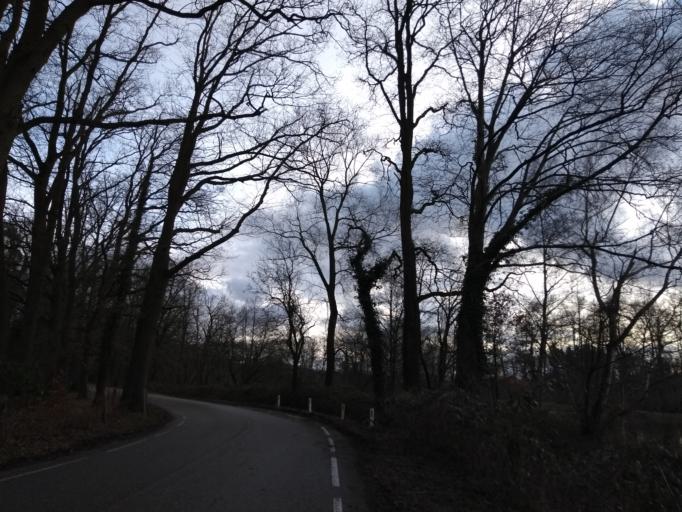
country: NL
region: Overijssel
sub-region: Gemeente Enschede
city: Enschede
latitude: 52.2540
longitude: 6.8817
